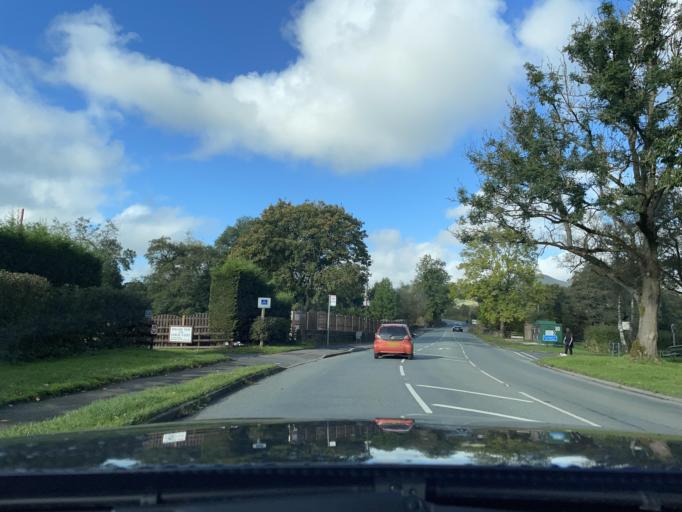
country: GB
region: England
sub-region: Derbyshire
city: Hope Valley
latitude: 53.3462
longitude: -1.7366
